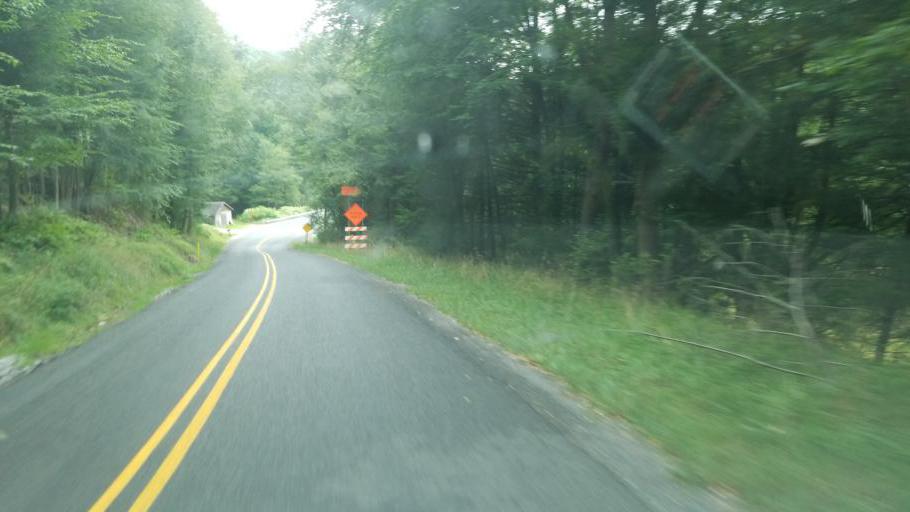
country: US
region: Pennsylvania
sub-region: Clarion County
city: Marianne
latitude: 41.1692
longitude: -79.4699
